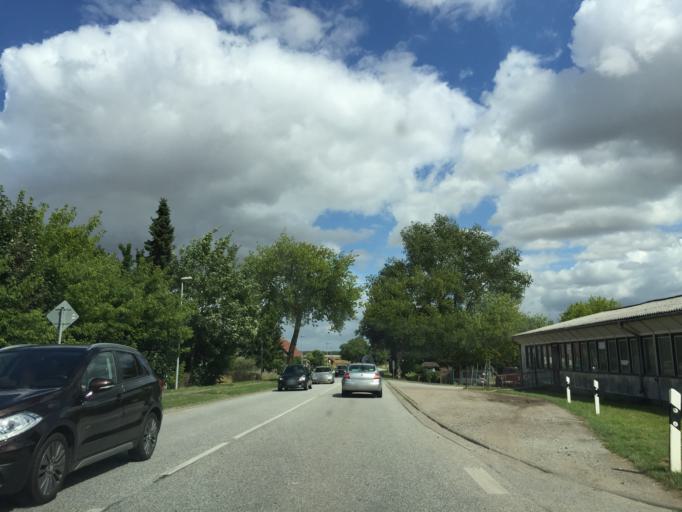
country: DE
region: Mecklenburg-Vorpommern
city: Rosenow
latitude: 53.6251
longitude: 13.0603
